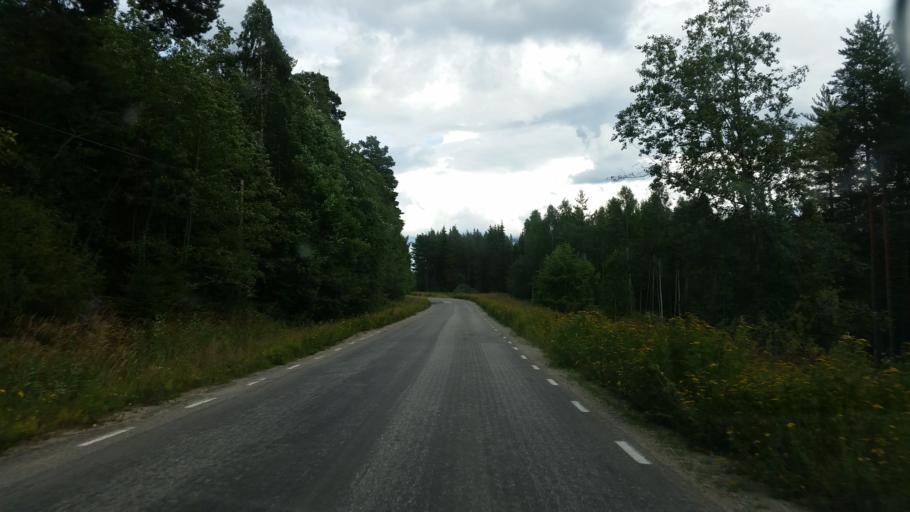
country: SE
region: Gaevleborg
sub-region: Hudiksvalls Kommun
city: Delsbo
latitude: 61.9126
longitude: 16.5803
